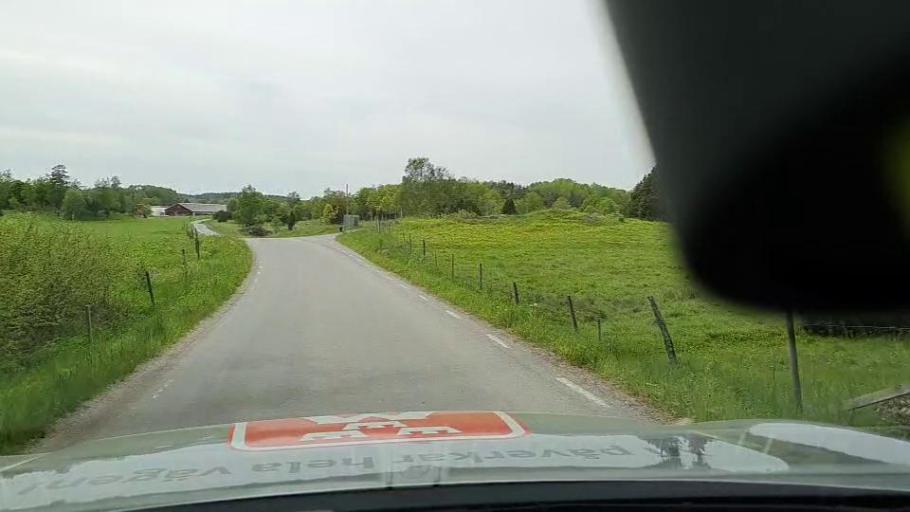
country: SE
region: Soedermanland
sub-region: Flens Kommun
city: Halleforsnas
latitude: 59.1014
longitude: 16.5037
